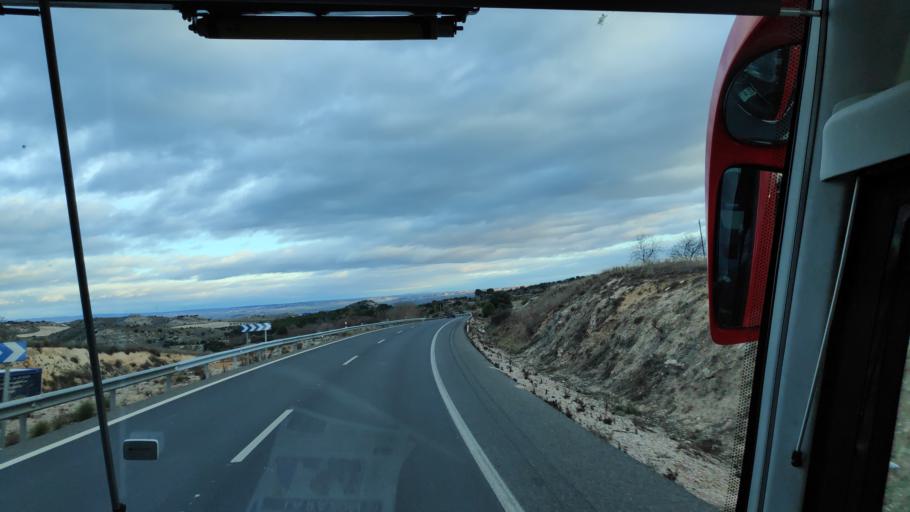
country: ES
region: Madrid
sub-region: Provincia de Madrid
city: Villarejo de Salvanes
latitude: 40.1506
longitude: -3.2344
